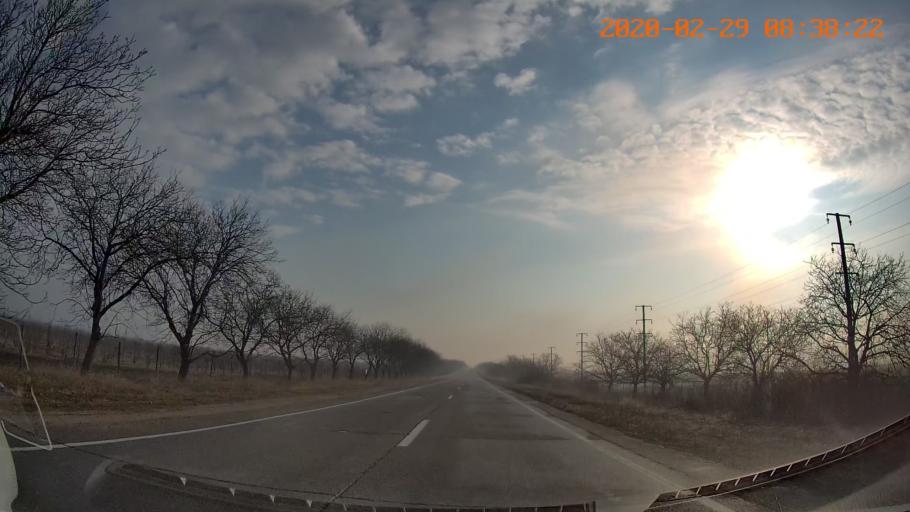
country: MD
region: Anenii Noi
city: Varnita
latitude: 46.9217
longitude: 29.3771
